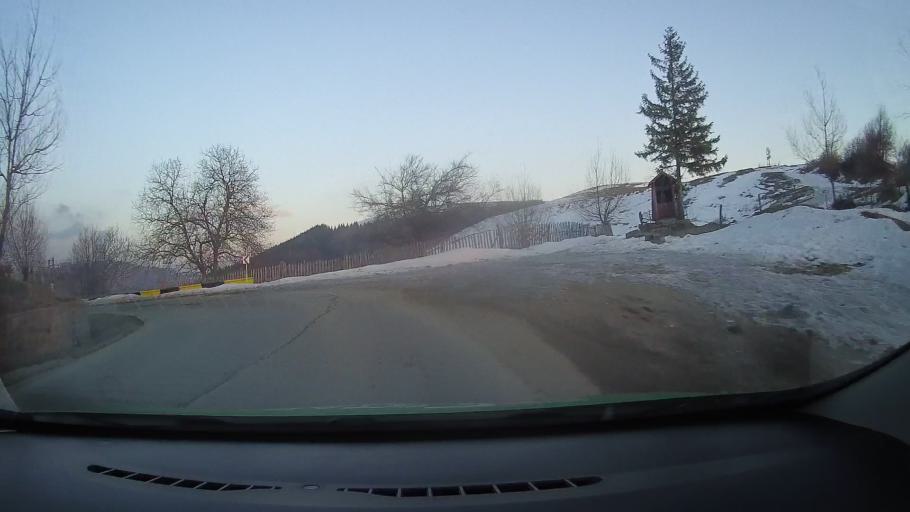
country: RO
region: Prahova
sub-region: Comuna Comarnic
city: Poiana
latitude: 45.2643
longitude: 25.6711
